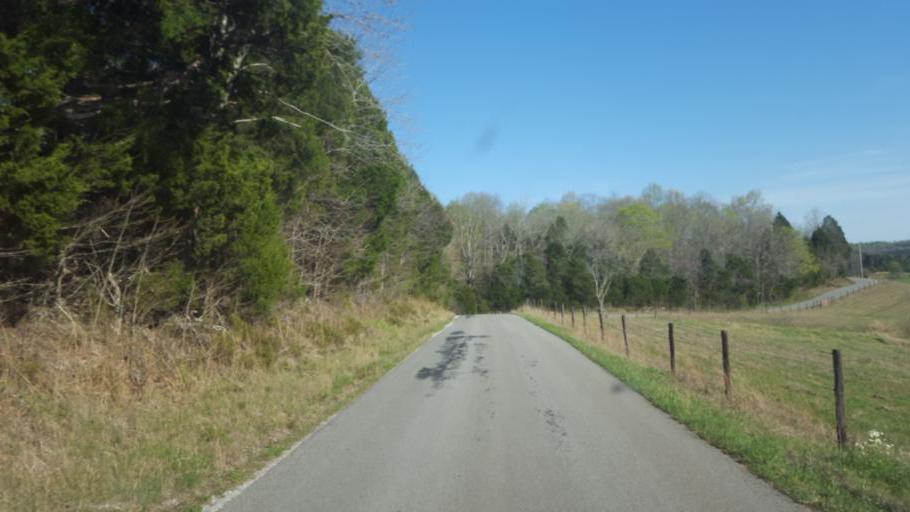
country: US
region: Kentucky
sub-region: Barren County
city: Cave City
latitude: 37.2005
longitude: -86.0167
